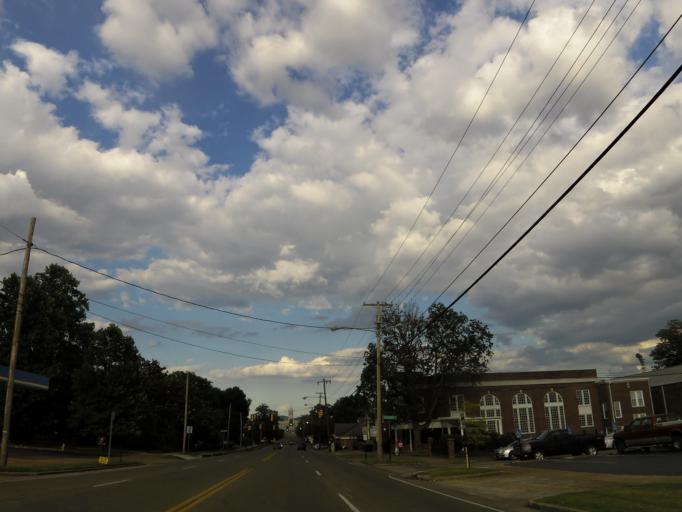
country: US
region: Tennessee
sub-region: Maury County
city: Columbia
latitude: 35.6156
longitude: -87.0412
